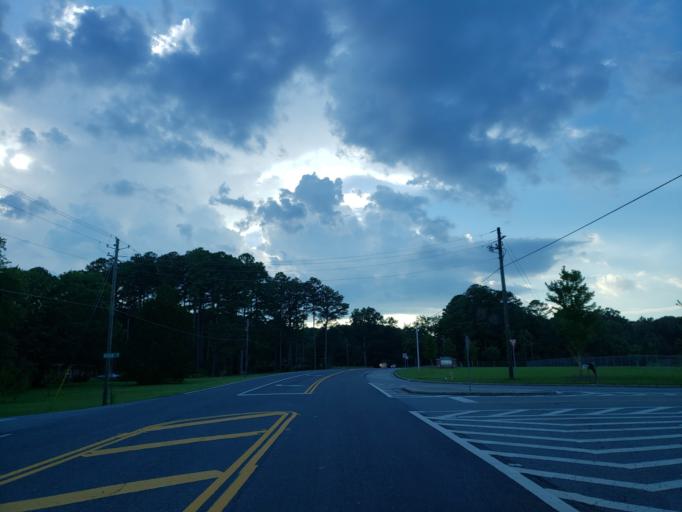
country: US
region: Georgia
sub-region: Bartow County
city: Cartersville
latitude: 34.2026
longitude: -84.7442
